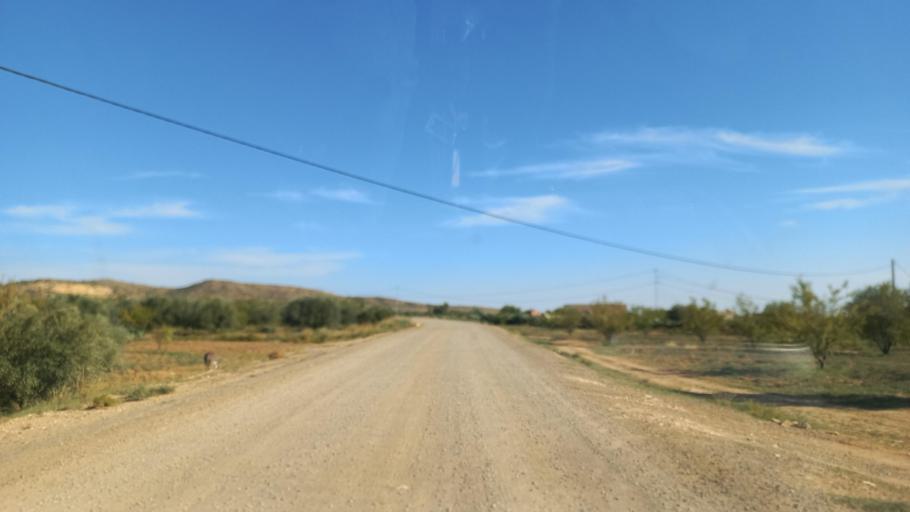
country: TN
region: Al Qasrayn
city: Sbiba
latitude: 35.2947
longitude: 9.1070
